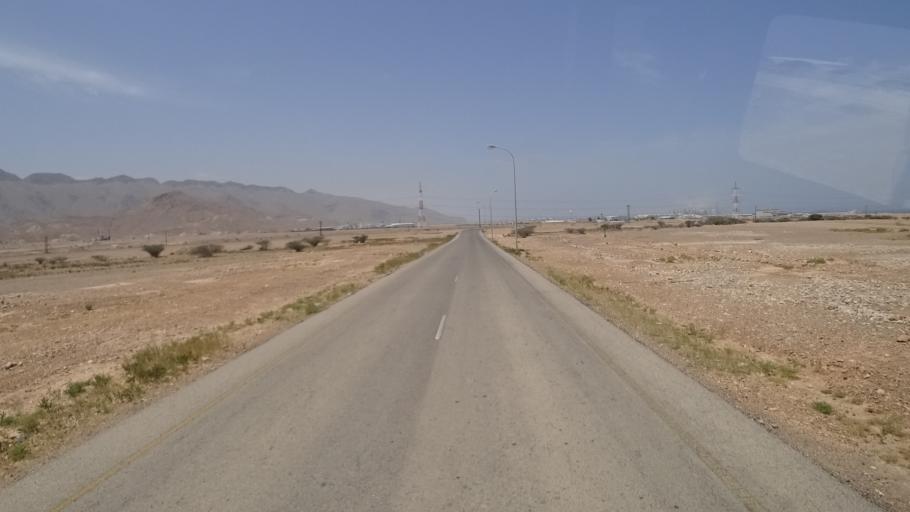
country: OM
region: Ash Sharqiyah
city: Sur
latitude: 22.6054
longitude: 59.4355
